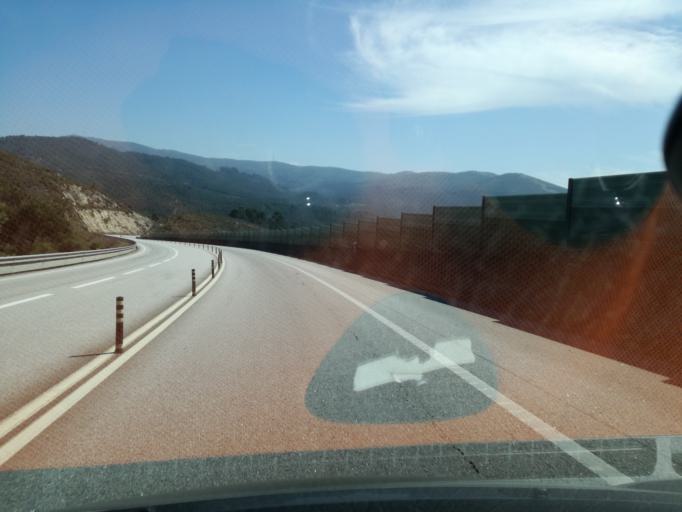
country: PT
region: Viana do Castelo
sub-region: Vila Nova de Cerveira
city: Vila Nova de Cerveira
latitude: 41.8961
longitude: -8.7820
